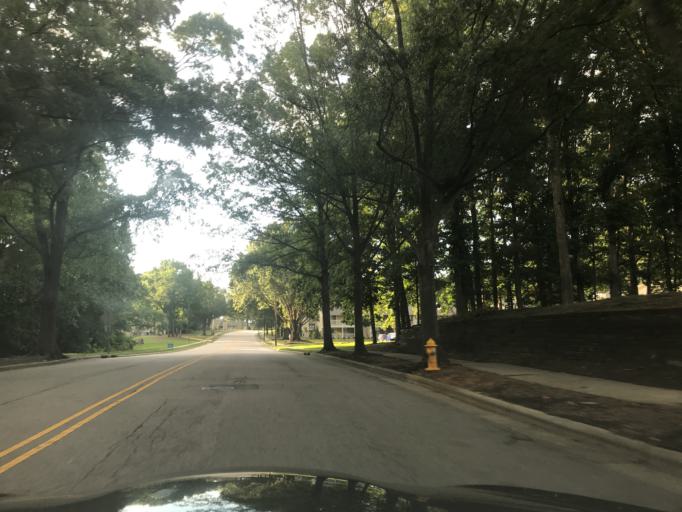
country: US
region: North Carolina
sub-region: Wake County
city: West Raleigh
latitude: 35.8632
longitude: -78.6303
